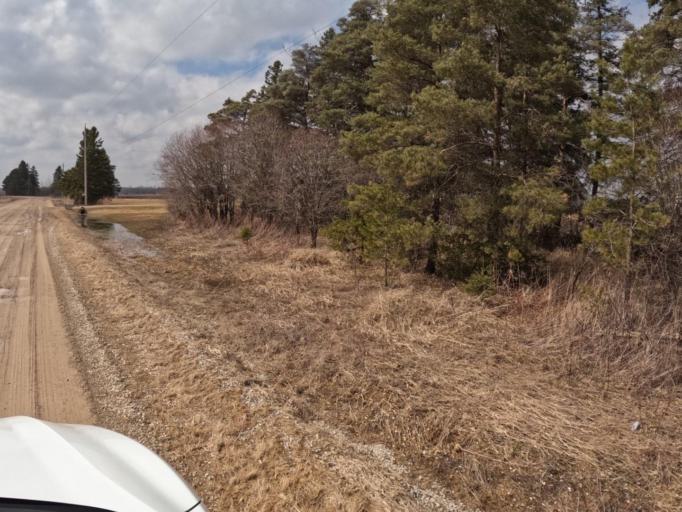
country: CA
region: Ontario
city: Shelburne
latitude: 44.0234
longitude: -80.2846
